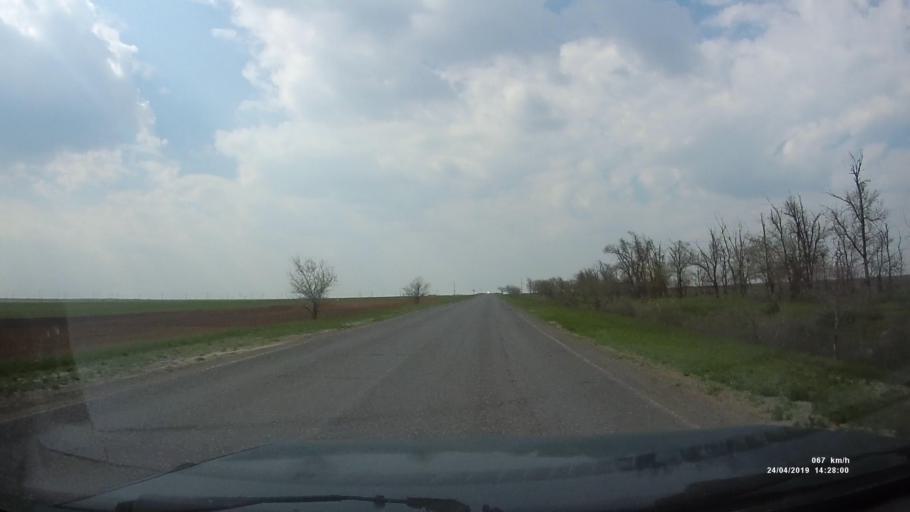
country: RU
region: Kalmykiya
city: Arshan'
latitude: 46.3352
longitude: 44.0339
